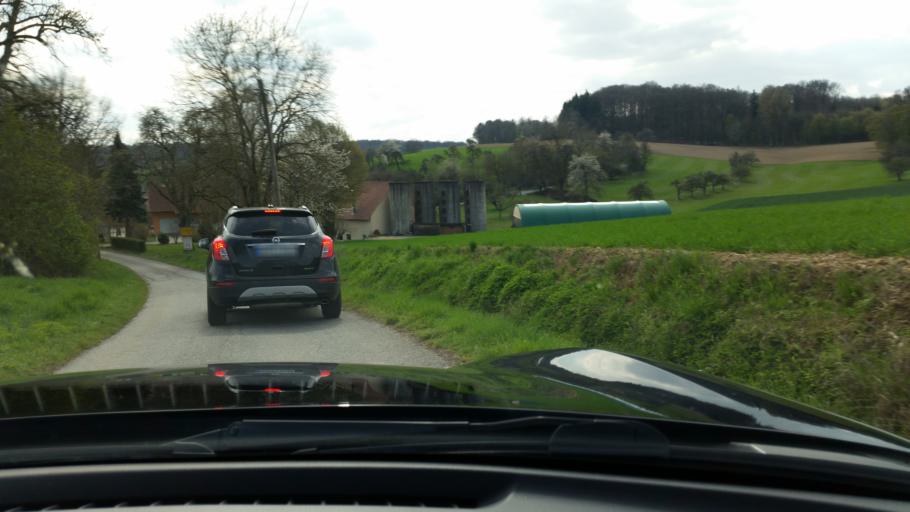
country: DE
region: Baden-Wuerttemberg
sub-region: Regierungsbezirk Stuttgart
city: Widdern
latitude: 49.3567
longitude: 9.4239
